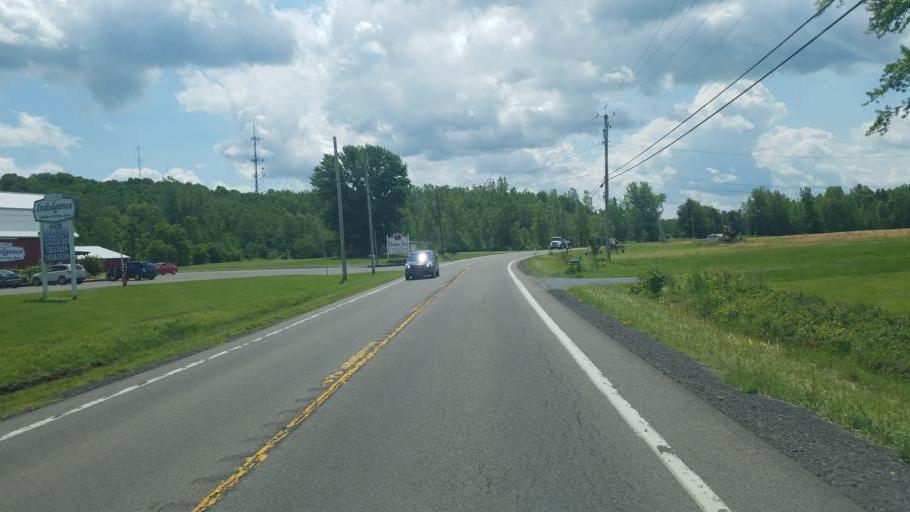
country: US
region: New York
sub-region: Wayne County
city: Wolcott
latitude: 43.1680
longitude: -76.8801
